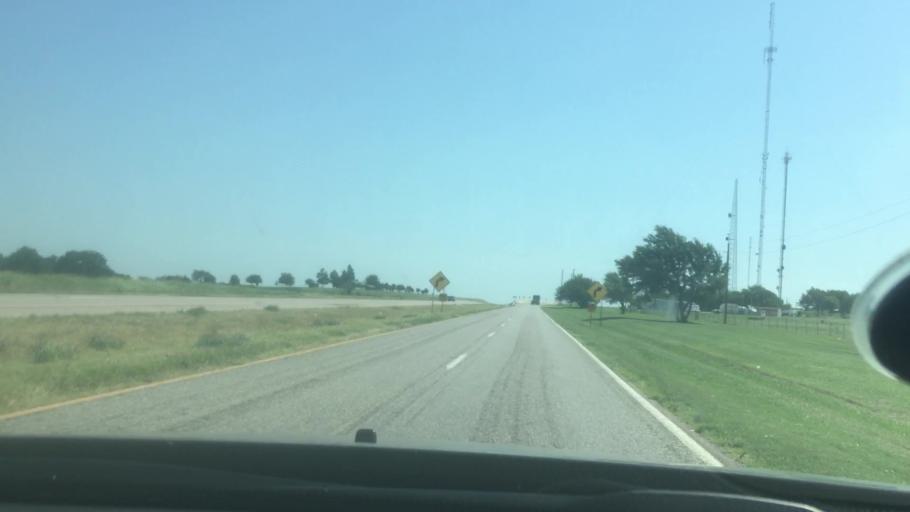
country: US
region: Oklahoma
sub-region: Pontotoc County
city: Ada
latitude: 34.6821
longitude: -96.7660
